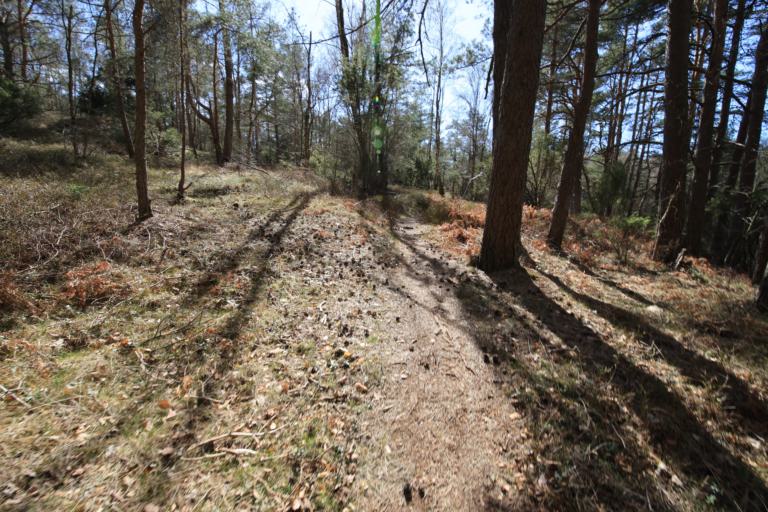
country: SE
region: Halland
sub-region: Varbergs Kommun
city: Varberg
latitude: 57.1783
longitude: 12.2367
